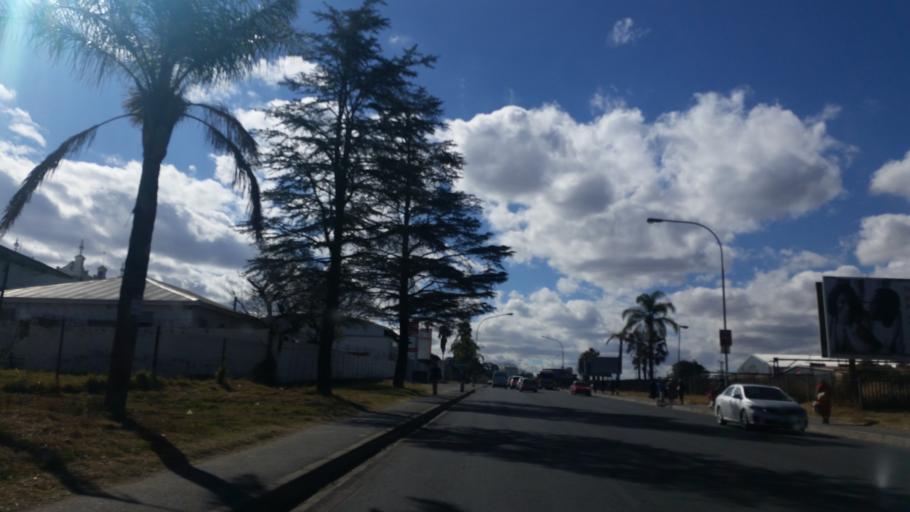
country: ZA
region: KwaZulu-Natal
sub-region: uThukela District Municipality
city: Ladysmith
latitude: -28.5554
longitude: 29.7853
